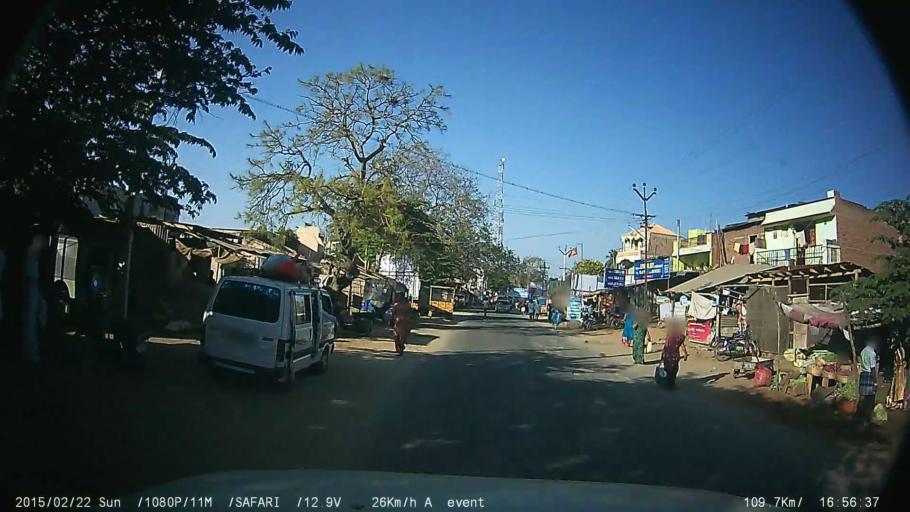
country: IN
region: Tamil Nadu
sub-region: Theni
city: Gudalur
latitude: 9.6804
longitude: 77.2443
